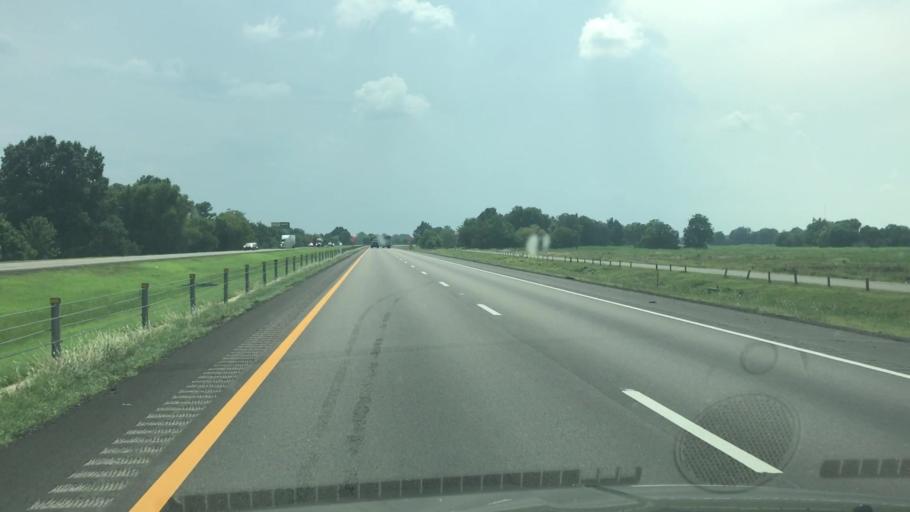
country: US
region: Arkansas
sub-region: Crittenden County
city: Earle
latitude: 35.1385
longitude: -90.4289
